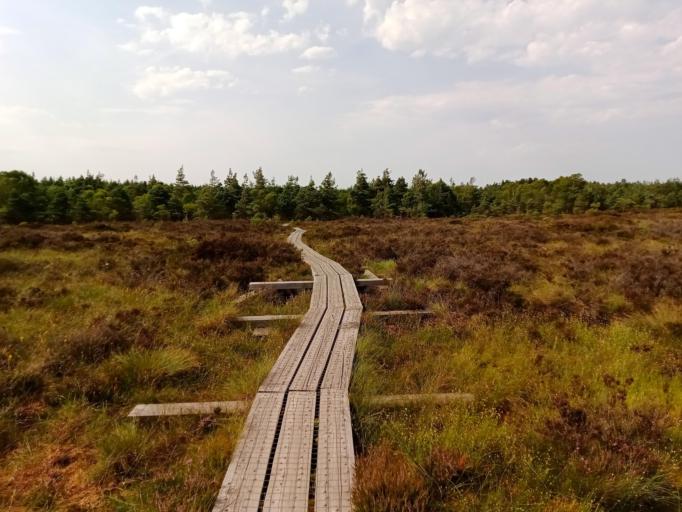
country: IE
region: Leinster
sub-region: Laois
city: Abbeyleix
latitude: 52.8940
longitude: -7.3552
